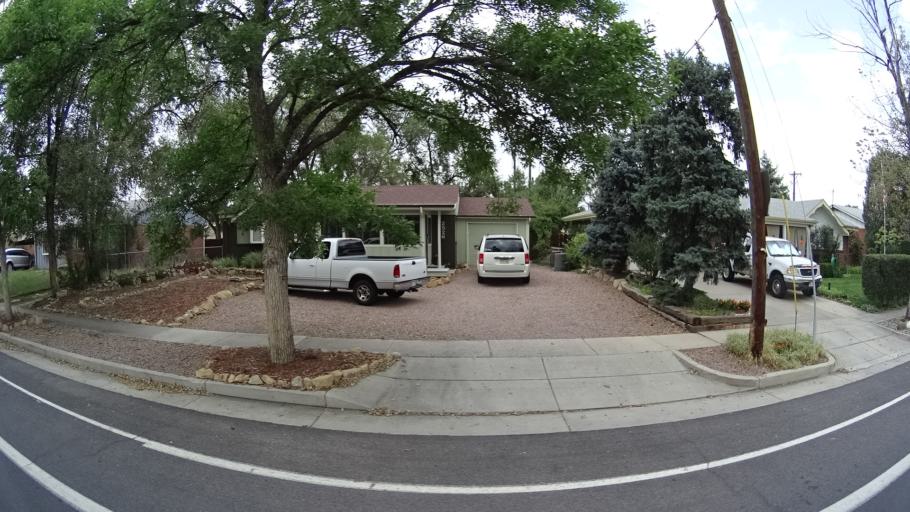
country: US
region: Colorado
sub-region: El Paso County
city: Colorado Springs
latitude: 38.8357
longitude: -104.7829
